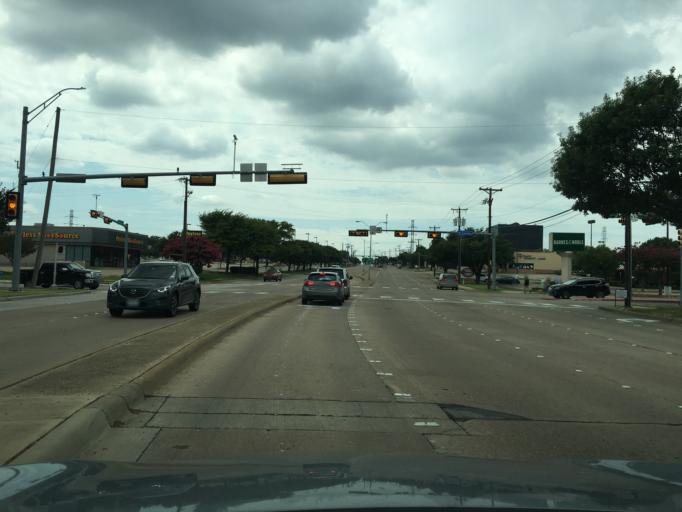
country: US
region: Texas
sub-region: Collin County
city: Plano
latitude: 33.0191
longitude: -96.7127
